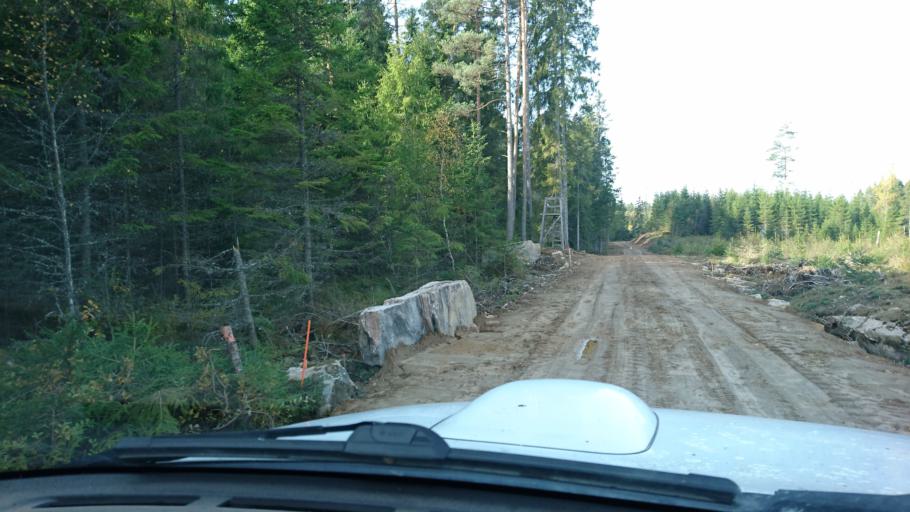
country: SE
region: Vaestra Goetaland
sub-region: Ulricehamns Kommun
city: Ulricehamn
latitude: 57.9375
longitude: 13.5540
